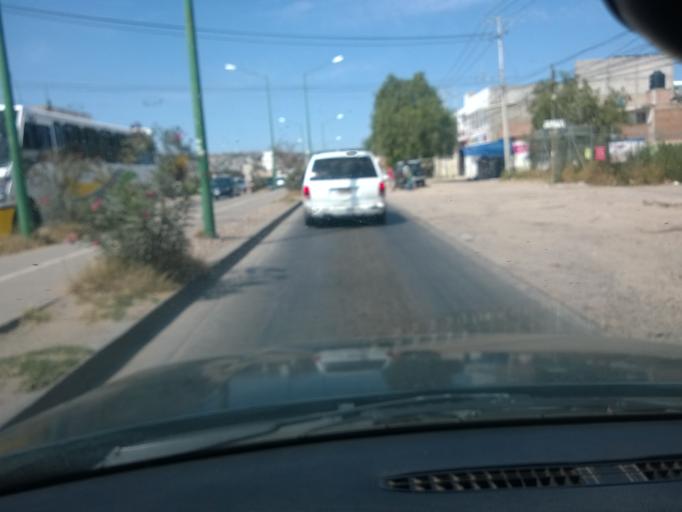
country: MX
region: Guanajuato
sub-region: Leon
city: Ejido la Joya
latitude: 21.1383
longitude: -101.7296
